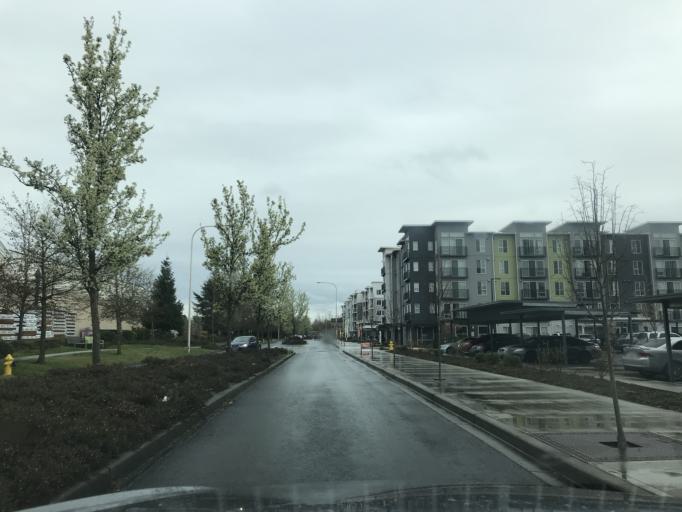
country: US
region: Washington
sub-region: King County
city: Auburn
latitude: 47.3190
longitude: -122.2288
